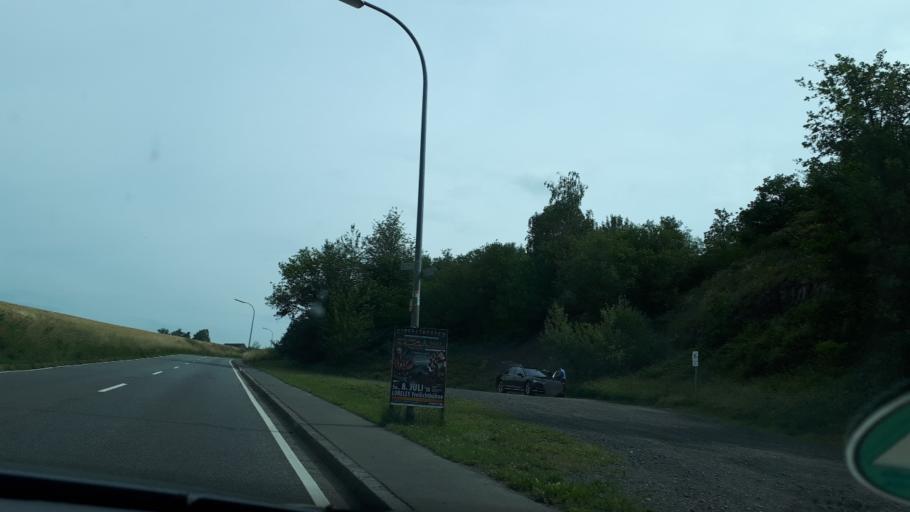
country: DE
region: Rheinland-Pfalz
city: Trimbs
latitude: 50.3293
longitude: 7.3030
